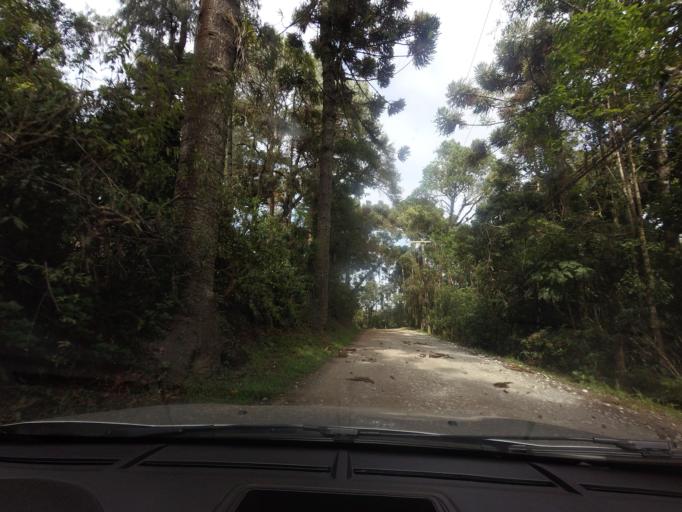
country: BR
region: Sao Paulo
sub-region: Campos Do Jordao
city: Campos do Jordao
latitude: -22.7694
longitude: -45.6026
